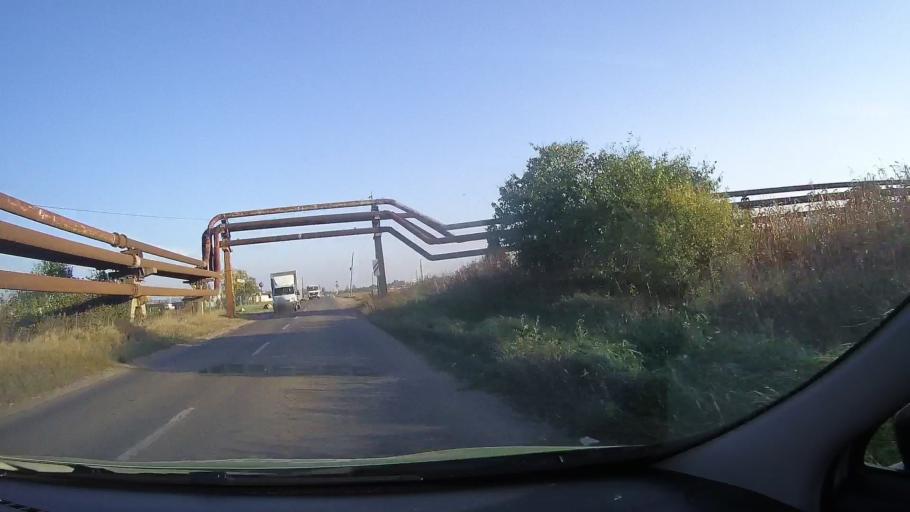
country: RO
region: Bihor
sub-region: Comuna Bors
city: Santion
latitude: 47.1085
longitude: 21.8671
